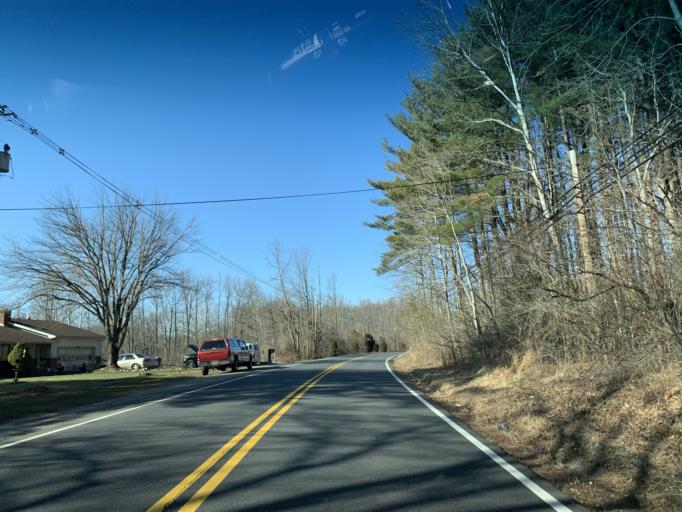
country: US
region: Maryland
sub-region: Cecil County
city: Elkton
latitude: 39.6356
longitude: -75.8636
